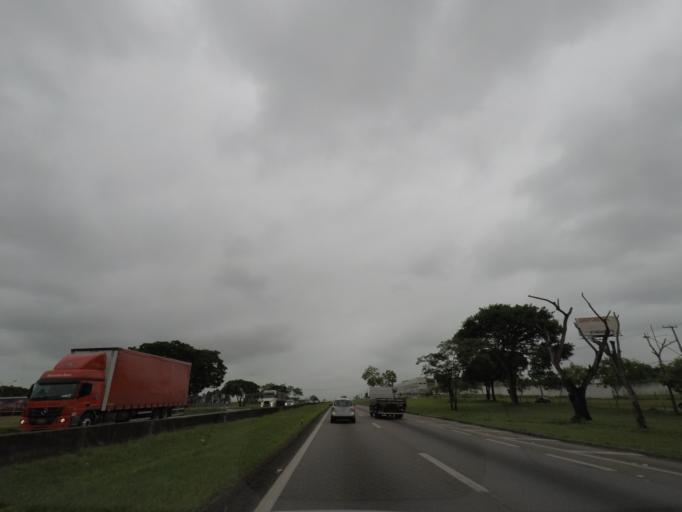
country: BR
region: Sao Paulo
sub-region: Cacapava
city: Cacapava
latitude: -23.1530
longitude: -45.7872
